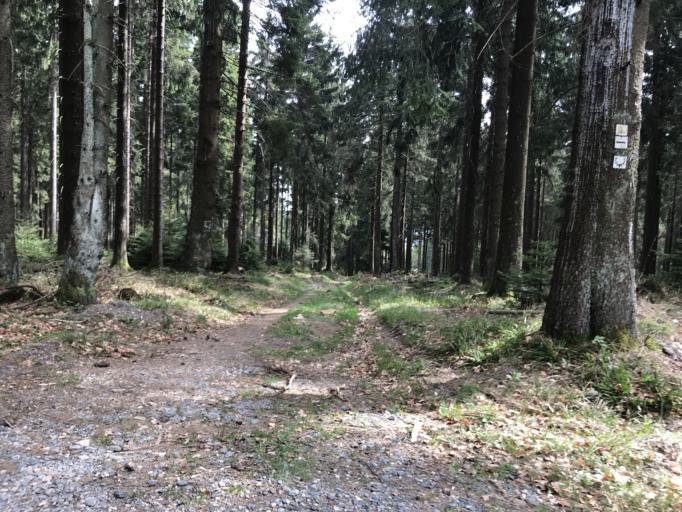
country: DE
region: Hesse
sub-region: Regierungsbezirk Darmstadt
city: Konigstein im Taunus
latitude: 50.2199
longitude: 8.4522
